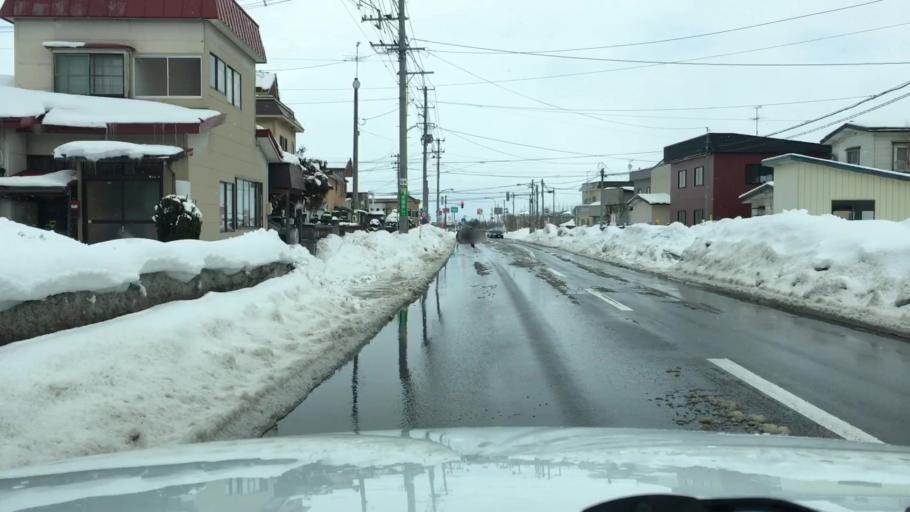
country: JP
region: Aomori
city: Hirosaki
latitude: 40.5811
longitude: 140.4963
